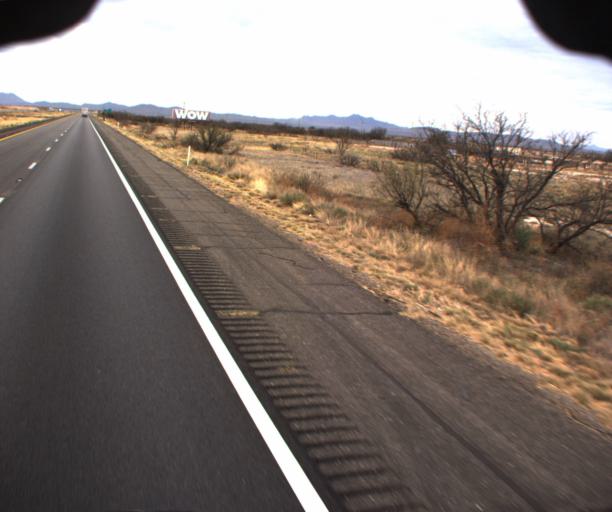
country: US
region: Arizona
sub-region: Cochise County
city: Willcox
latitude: 32.2314
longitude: -109.8714
